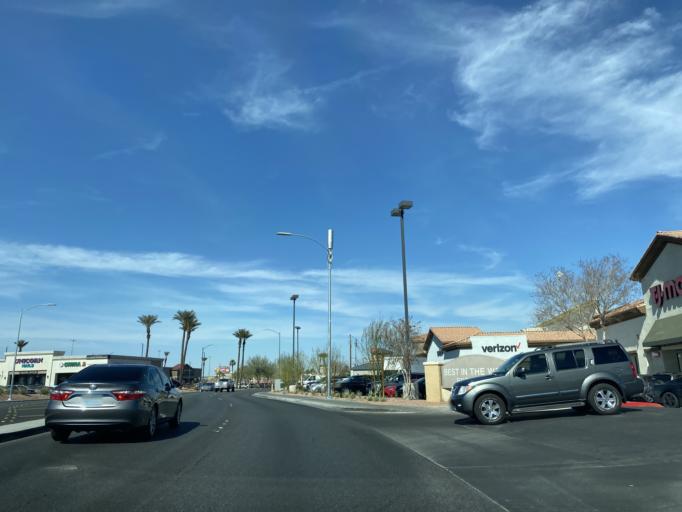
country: US
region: Nevada
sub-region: Clark County
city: Spring Valley
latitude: 36.1985
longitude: -115.2419
